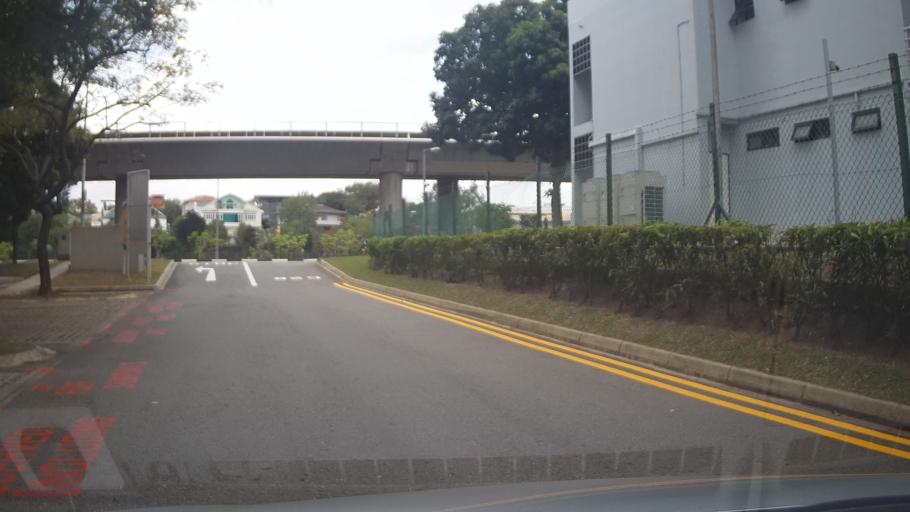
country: SG
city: Singapore
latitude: 1.3216
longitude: 103.7620
